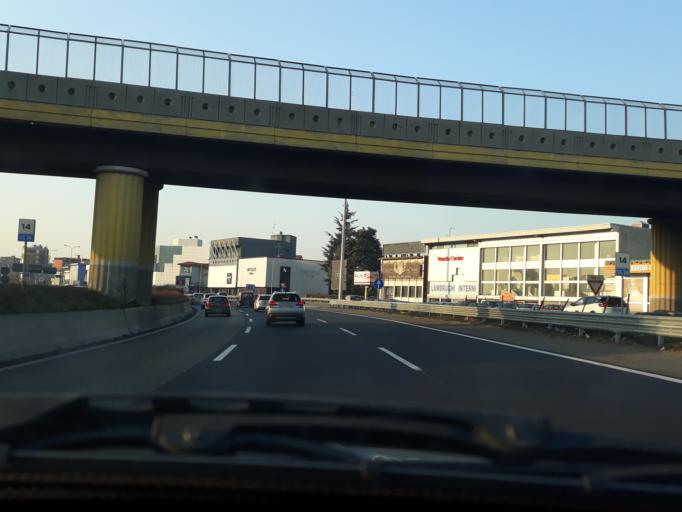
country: IT
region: Lombardy
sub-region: Provincia di Monza e Brianza
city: Lissone
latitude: 45.5972
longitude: 9.2424
